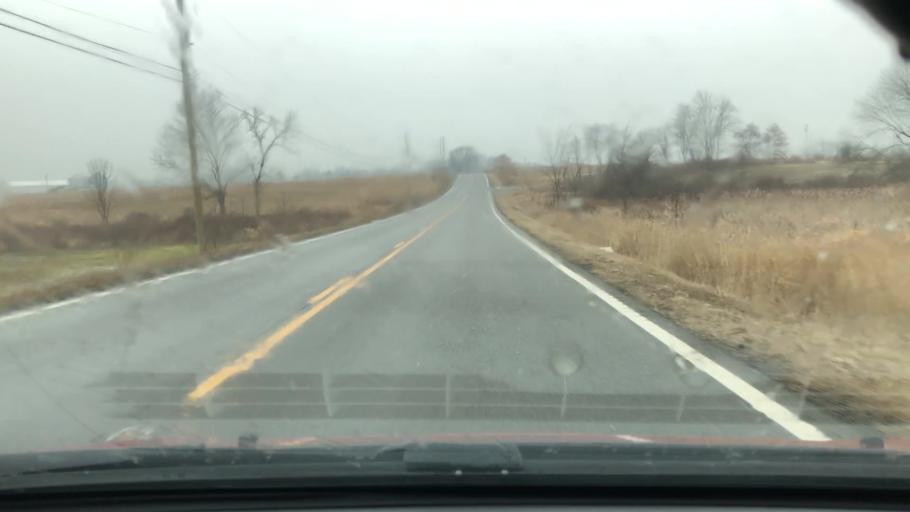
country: US
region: Ohio
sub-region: Wayne County
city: Rittman
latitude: 40.9322
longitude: -81.7552
